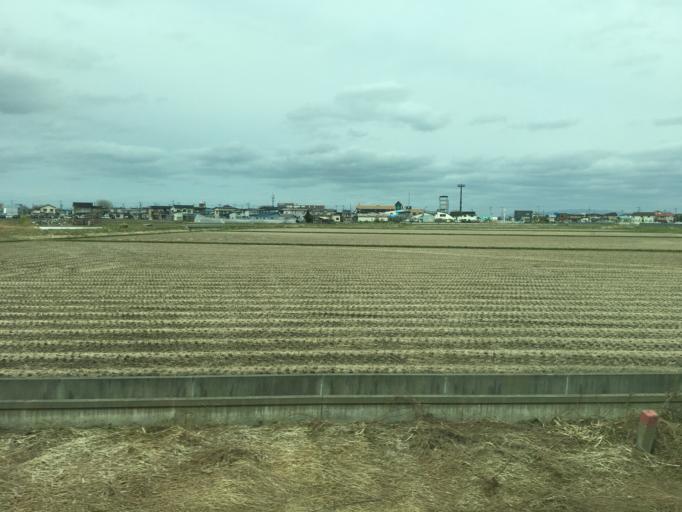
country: JP
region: Aomori
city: Shimokizukuri
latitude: 40.8053
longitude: 140.3969
